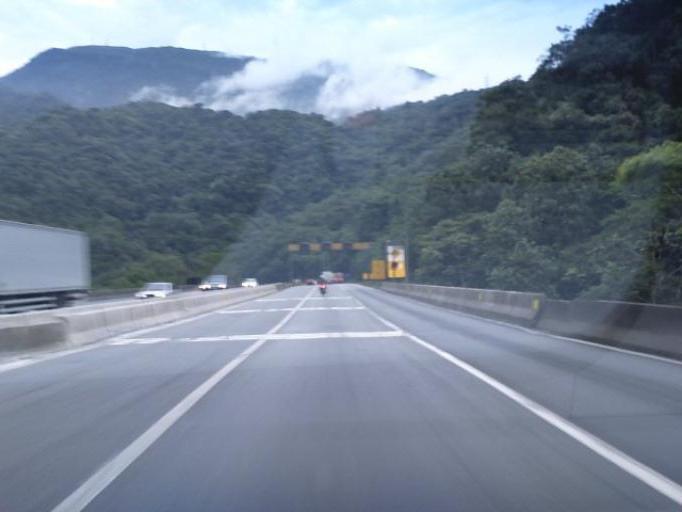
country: BR
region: Parana
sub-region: Guaratuba
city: Guaratuba
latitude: -25.8698
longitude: -48.9350
